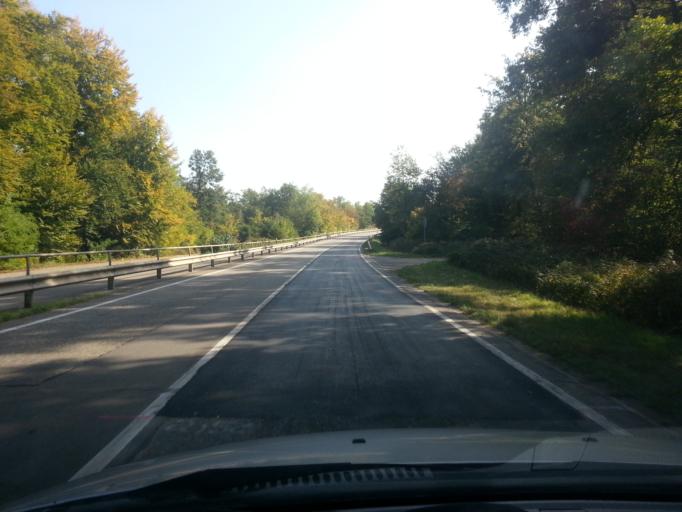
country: DE
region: Rheinland-Pfalz
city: Speyer
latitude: 49.3505
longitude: 8.4144
